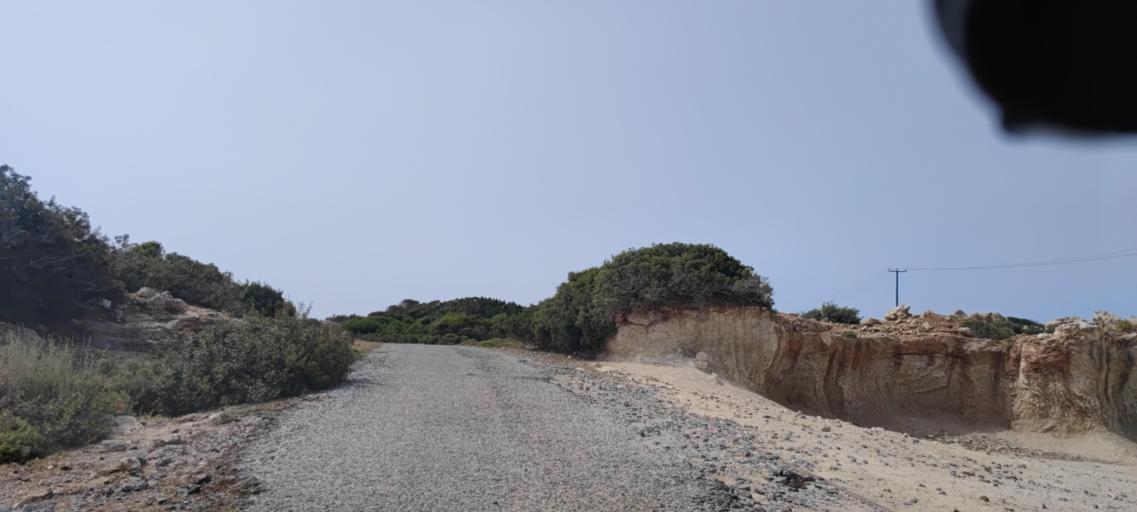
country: CY
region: Ammochostos
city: Rizokarpaso
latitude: 35.6662
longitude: 34.5716
